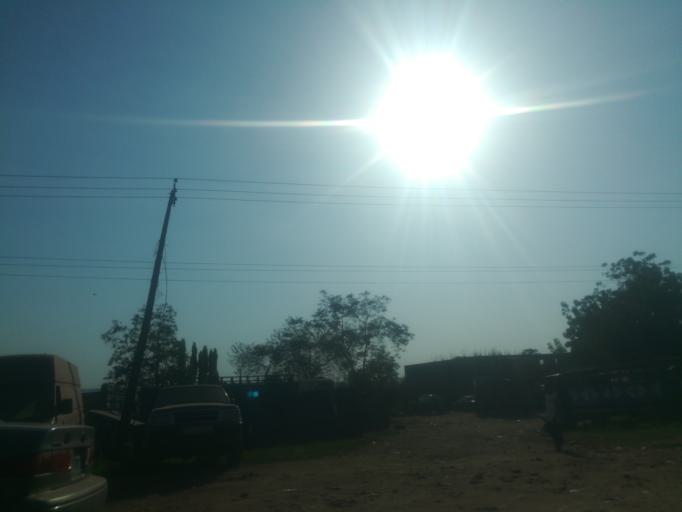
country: NG
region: Ogun
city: Abeokuta
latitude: 7.1785
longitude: 3.2852
